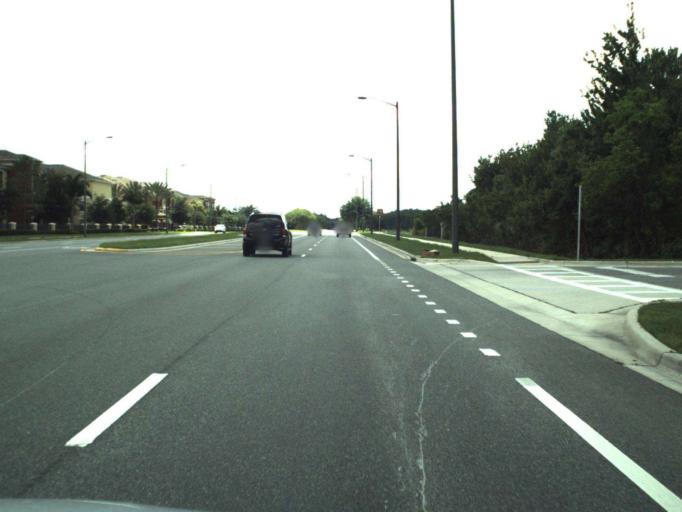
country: US
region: Florida
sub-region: Orange County
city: Conway
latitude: 28.4463
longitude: -81.2631
